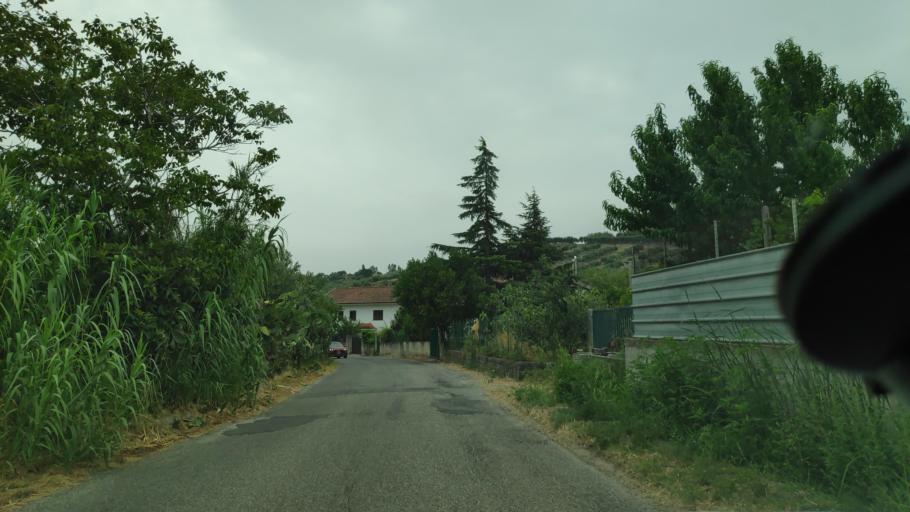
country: IT
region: Calabria
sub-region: Provincia di Catanzaro
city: Martelli-Laganosa
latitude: 38.6636
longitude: 16.5318
